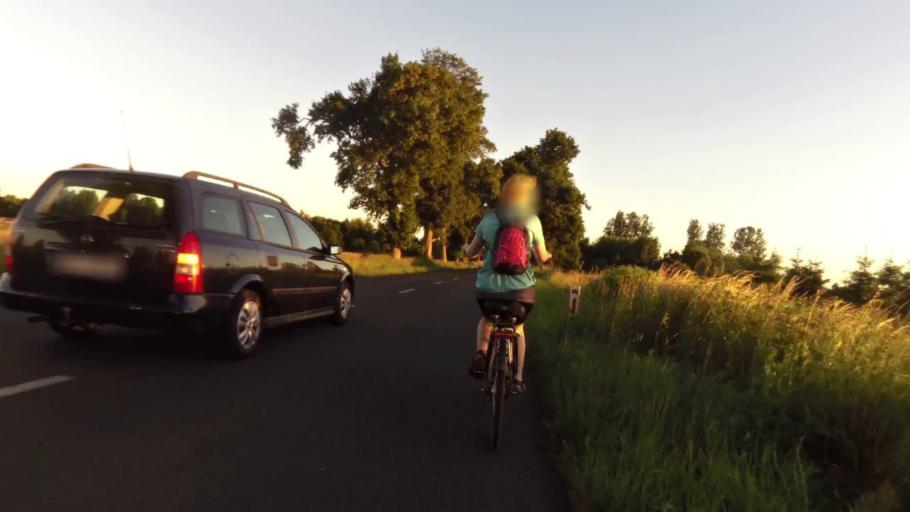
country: PL
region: West Pomeranian Voivodeship
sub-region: Powiat bialogardzki
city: Bialogard
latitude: 54.0171
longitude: 16.0095
